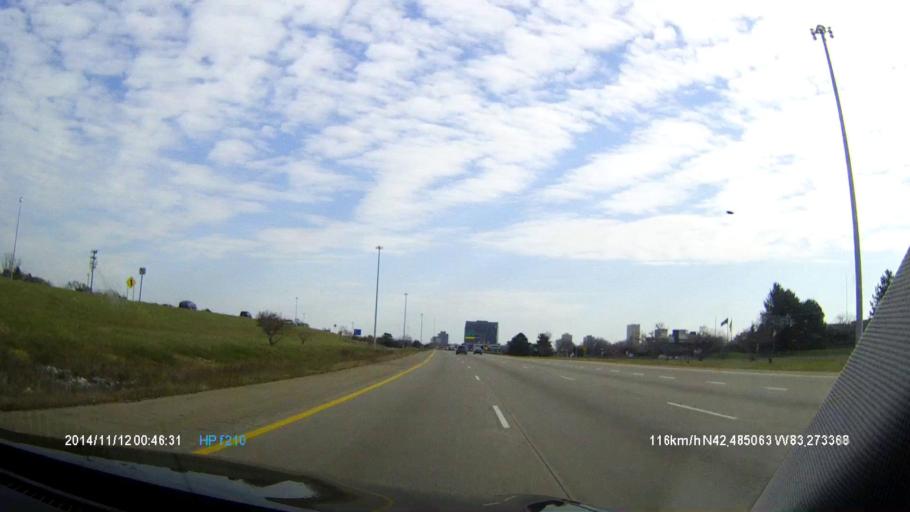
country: US
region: Michigan
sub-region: Oakland County
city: Bingham Farms
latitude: 42.4851
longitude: -83.2739
